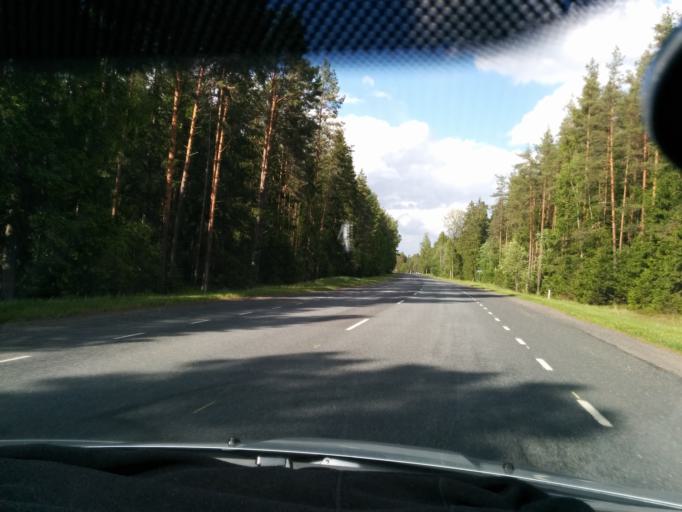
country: EE
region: Harju
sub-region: Loksa linn
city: Loksa
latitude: 59.5373
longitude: 25.7312
